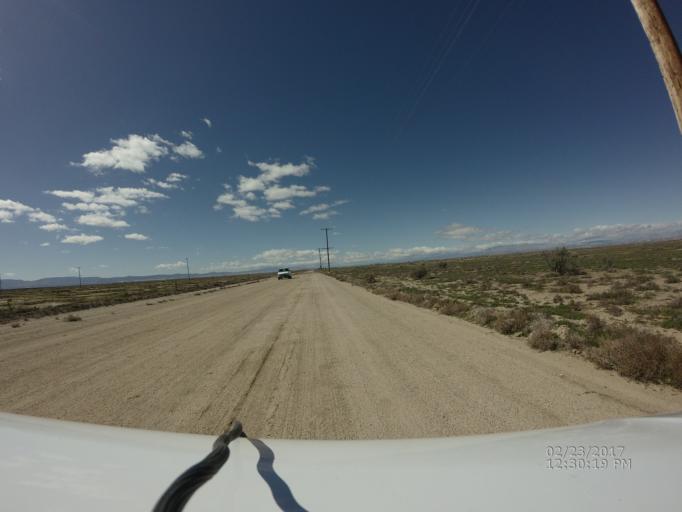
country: US
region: California
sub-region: Los Angeles County
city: Lancaster
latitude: 34.7484
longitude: -118.0487
